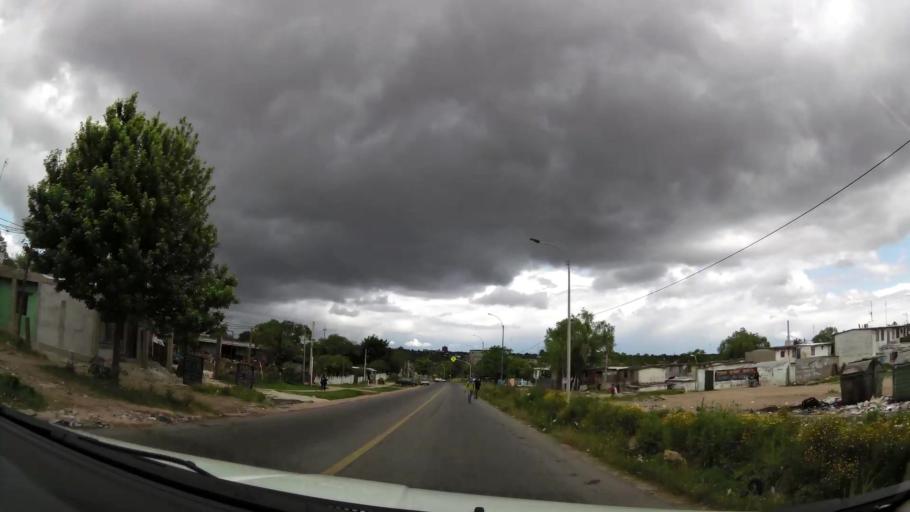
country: UY
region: Montevideo
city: Montevideo
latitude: -34.8342
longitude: -56.1683
